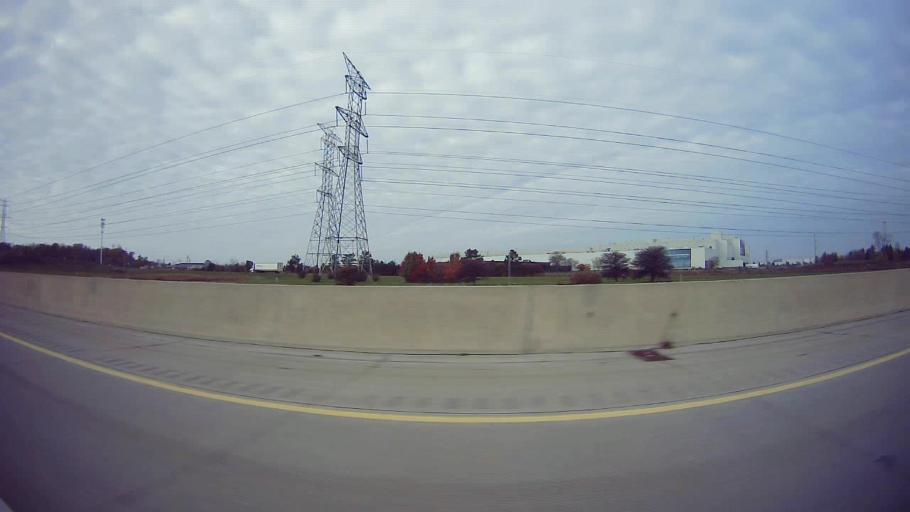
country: US
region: Michigan
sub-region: Wayne County
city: Rockwood
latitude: 42.0976
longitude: -83.2416
